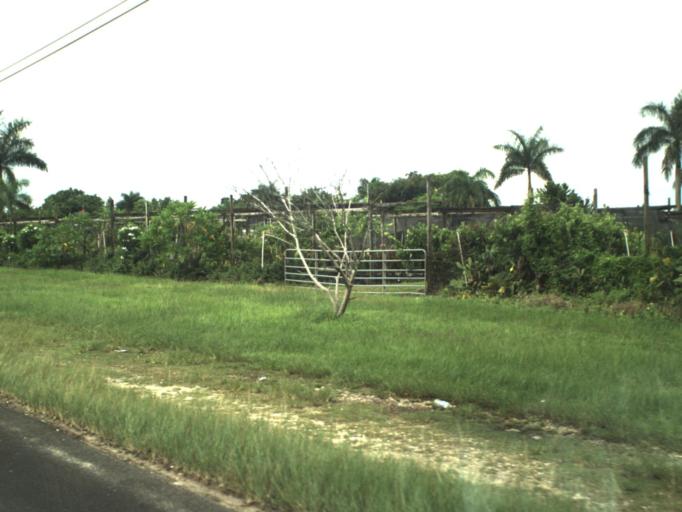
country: US
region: Florida
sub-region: Miami-Dade County
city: Richmond West
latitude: 25.5705
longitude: -80.4783
